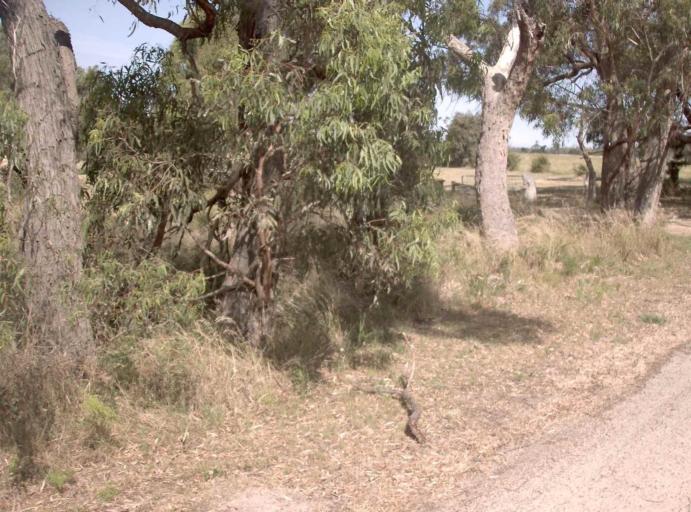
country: AU
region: Victoria
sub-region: Wellington
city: Sale
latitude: -38.2575
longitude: 147.1393
